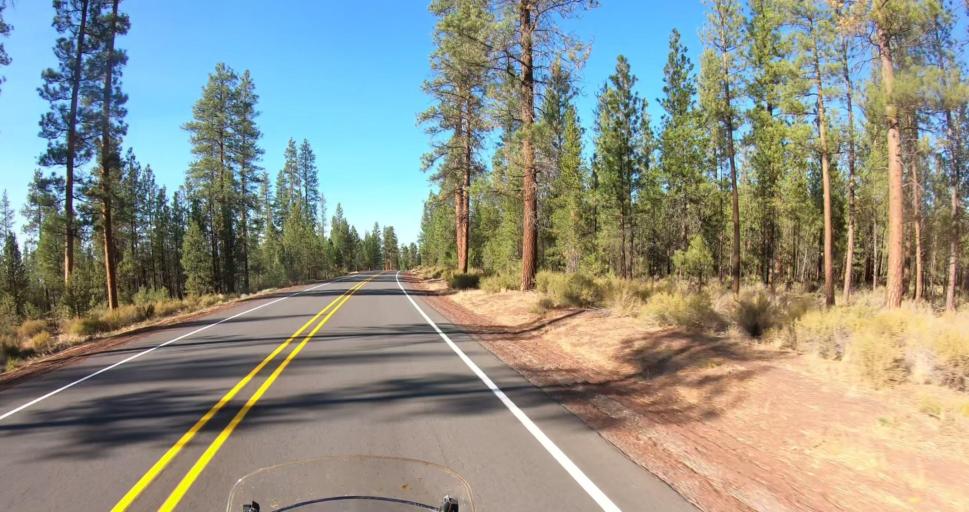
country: US
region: Oregon
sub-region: Deschutes County
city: La Pine
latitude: 43.4994
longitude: -121.4490
